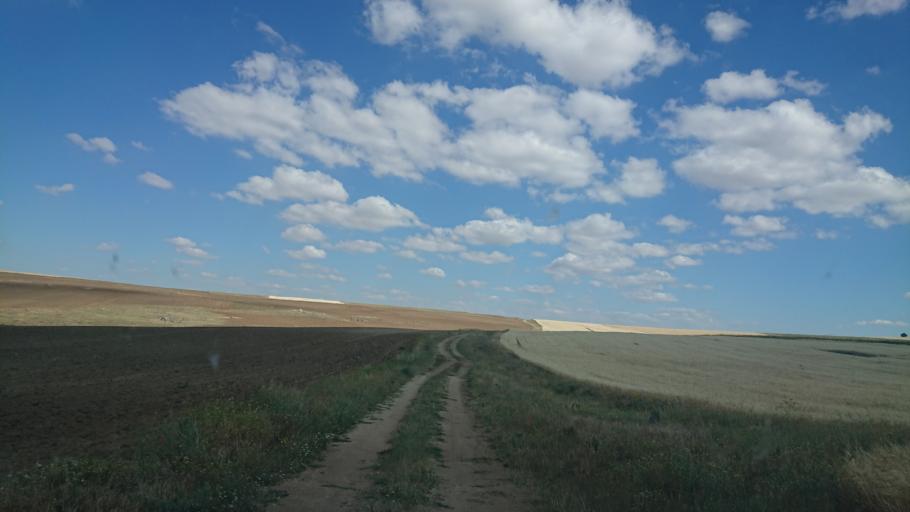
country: TR
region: Aksaray
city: Sariyahsi
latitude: 38.9344
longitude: 33.8434
